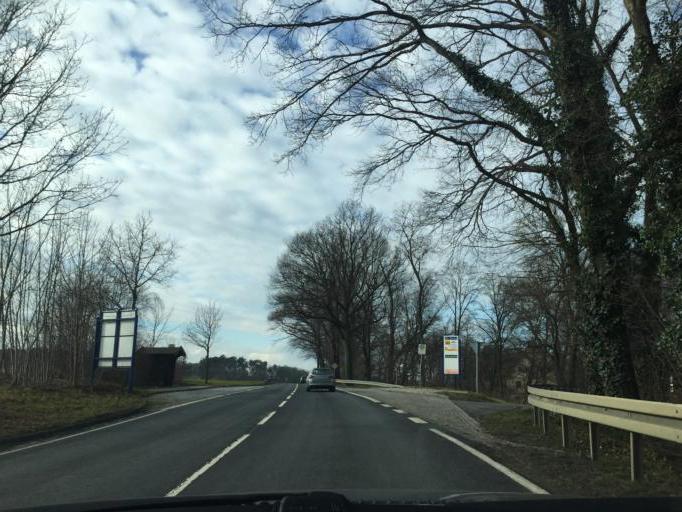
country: DE
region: Saxony
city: Radeburg
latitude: 51.2078
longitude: 13.7578
